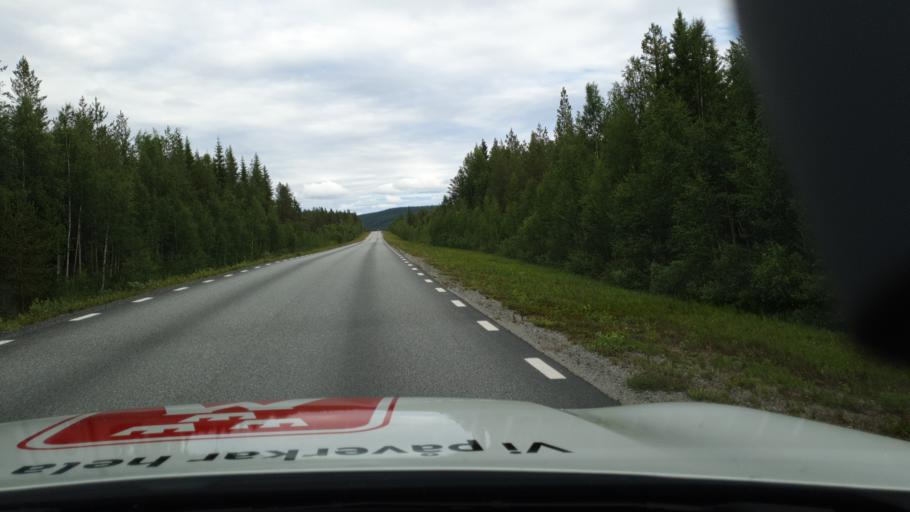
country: SE
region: Vaesterbotten
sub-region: Sorsele Kommun
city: Sorsele
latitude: 65.5275
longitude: 17.3905
